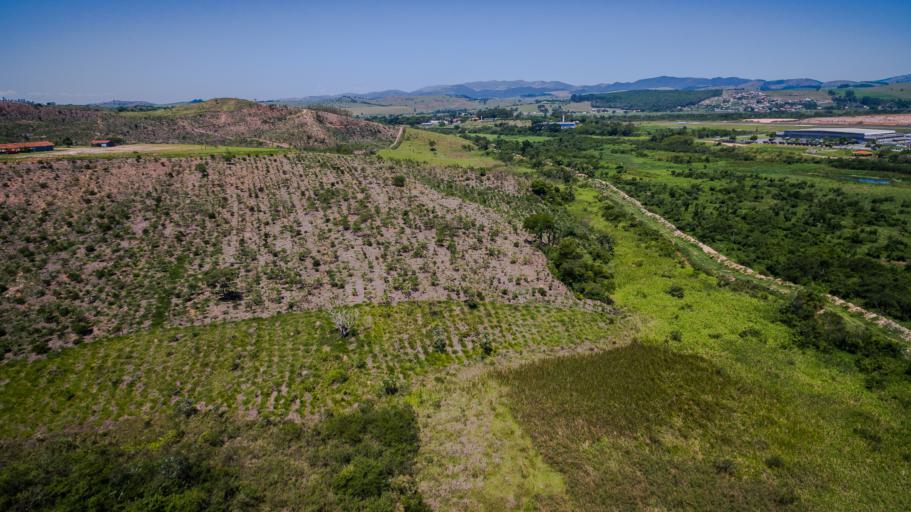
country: BR
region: Sao Paulo
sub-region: Taubate
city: Taubate
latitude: -23.0328
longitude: -45.5228
